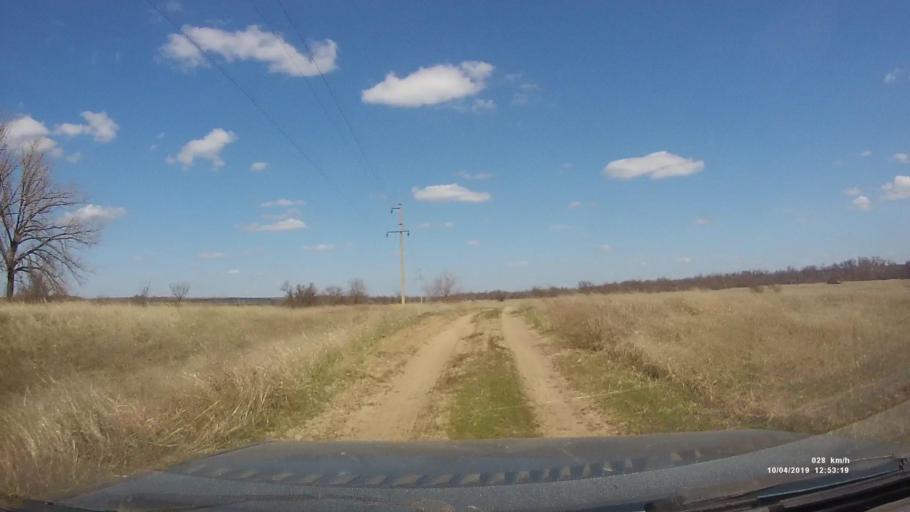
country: RU
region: Rostov
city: Masalovka
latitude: 48.3638
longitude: 40.2206
